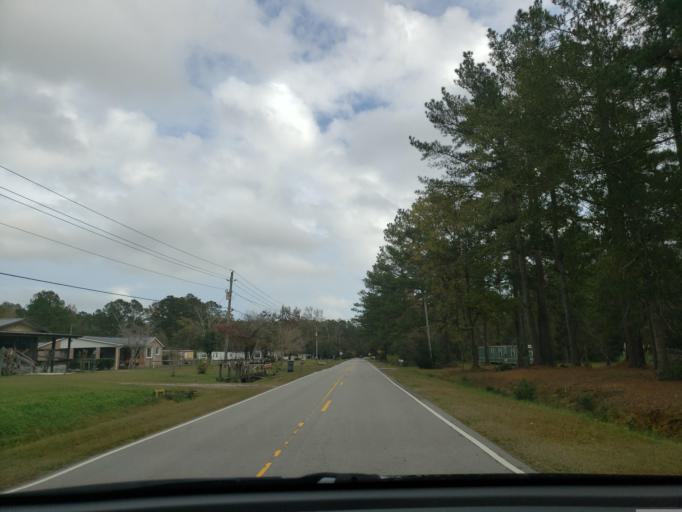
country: US
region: North Carolina
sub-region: Onslow County
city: Jacksonville
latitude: 34.7070
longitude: -77.5784
